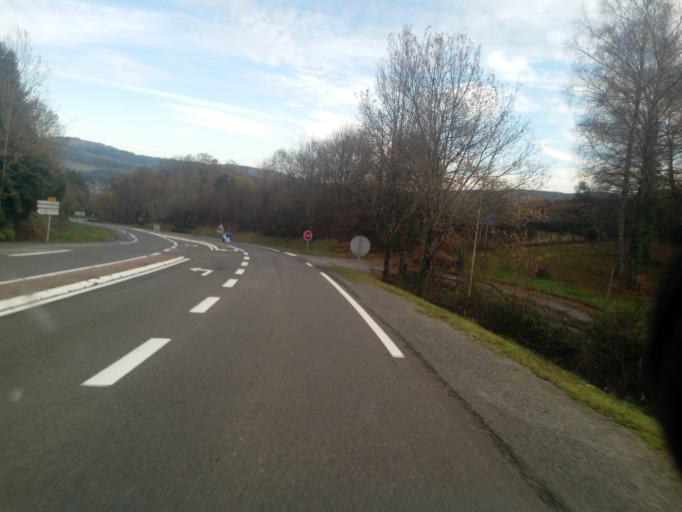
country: FR
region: Limousin
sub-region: Departement de la Haute-Vienne
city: Eymoutiers
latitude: 45.7394
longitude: 1.7248
